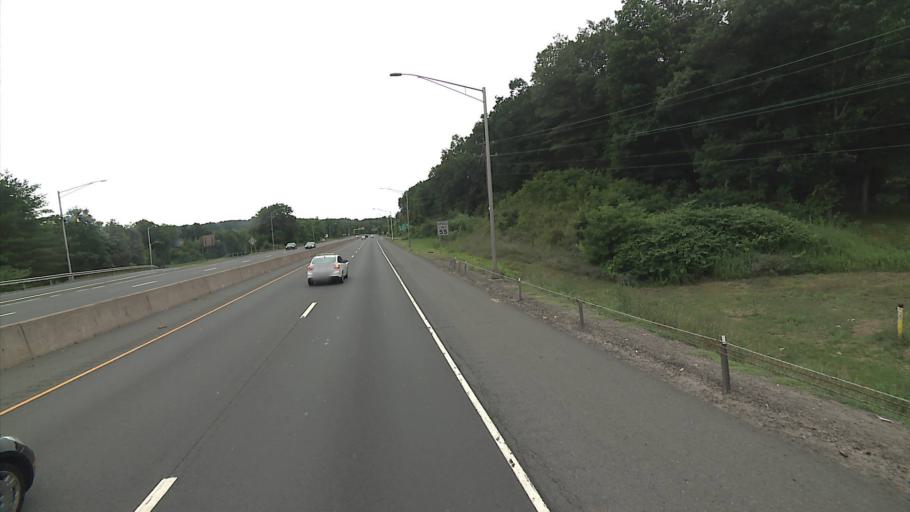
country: US
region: Connecticut
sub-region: New Haven County
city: Naugatuck
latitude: 41.5098
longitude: -73.0466
